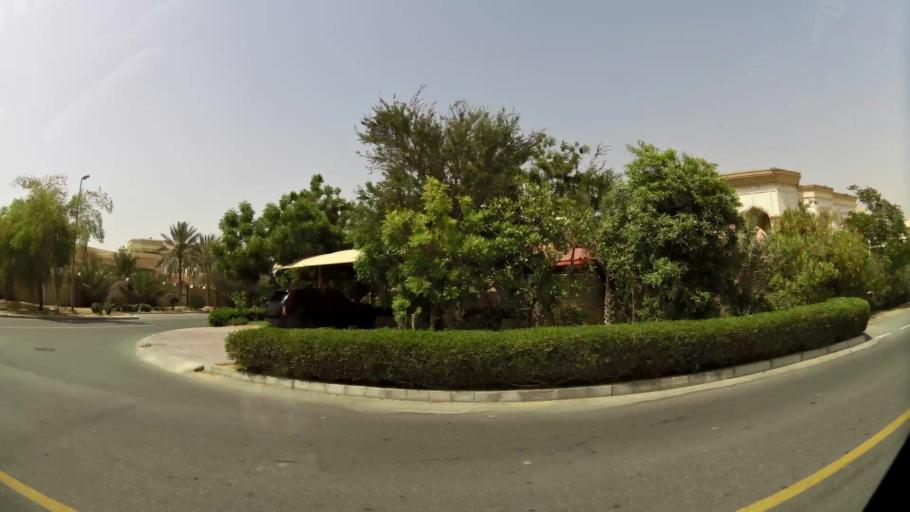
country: AE
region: Ash Shariqah
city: Sharjah
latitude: 25.2424
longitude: 55.4349
